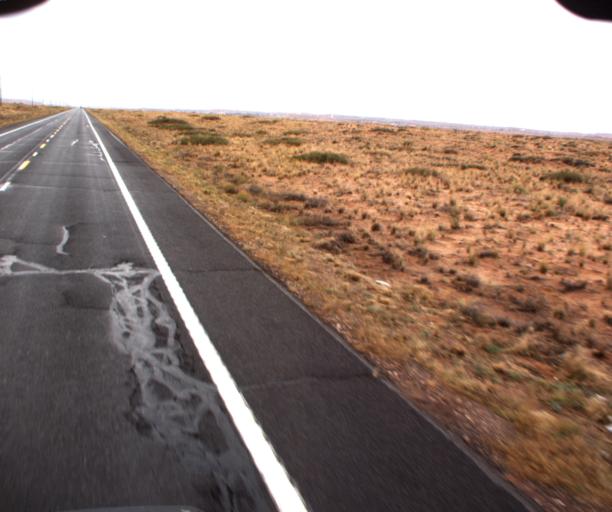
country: US
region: Arizona
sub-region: Coconino County
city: Tuba City
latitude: 36.1372
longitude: -111.1707
